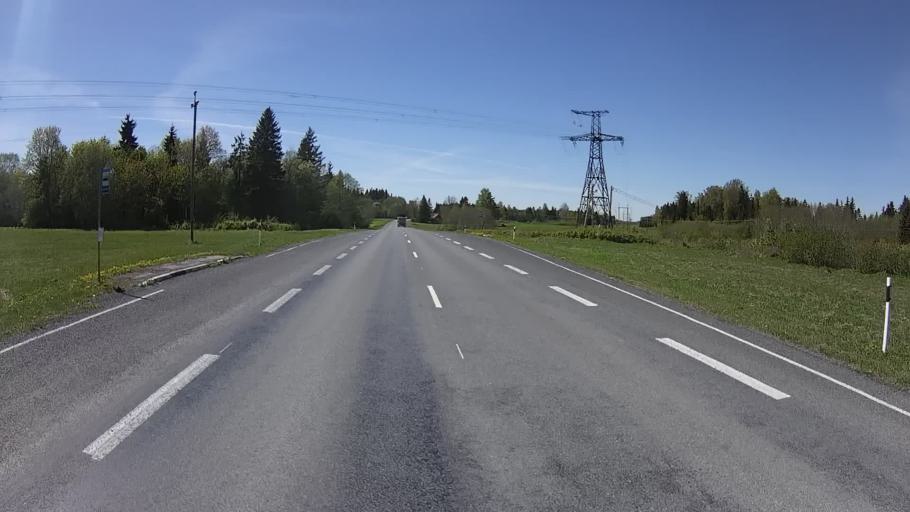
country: EE
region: Raplamaa
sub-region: Kehtna vald
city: Kehtna
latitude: 59.0401
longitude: 25.0859
